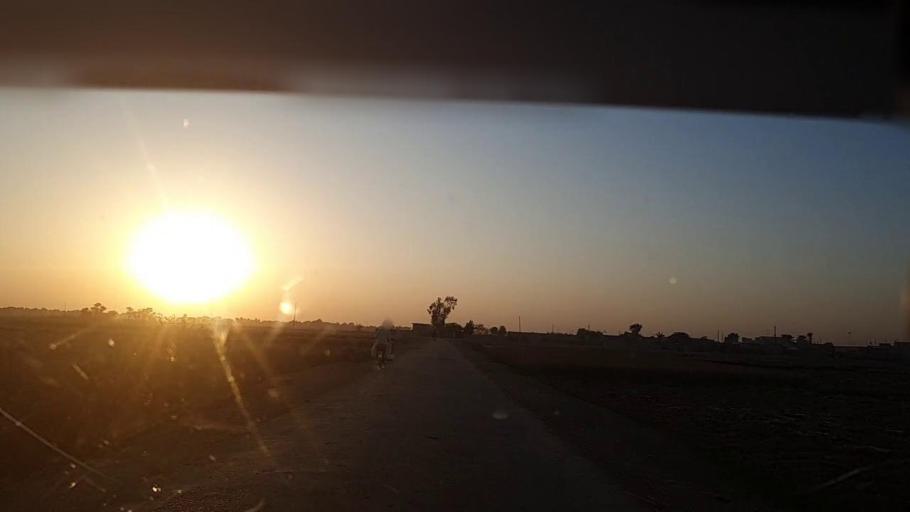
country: PK
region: Sindh
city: Ratodero
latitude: 27.8914
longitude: 68.2384
